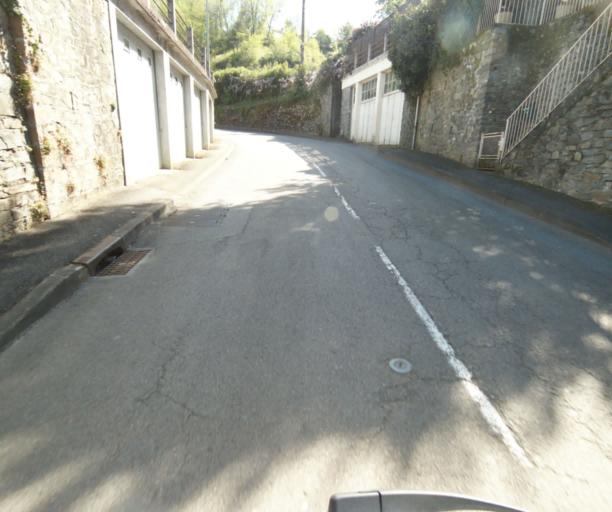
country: FR
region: Limousin
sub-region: Departement de la Correze
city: Tulle
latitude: 45.2652
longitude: 1.7737
